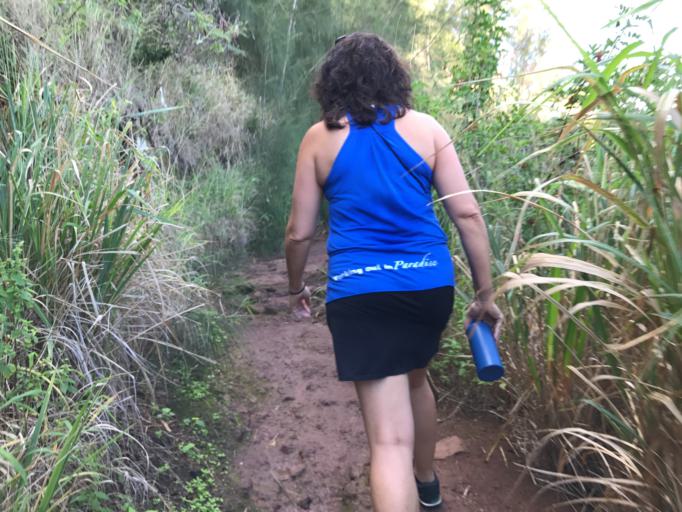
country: US
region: Hawaii
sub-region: Honolulu County
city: Mokuleia
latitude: 21.5720
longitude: -158.2093
